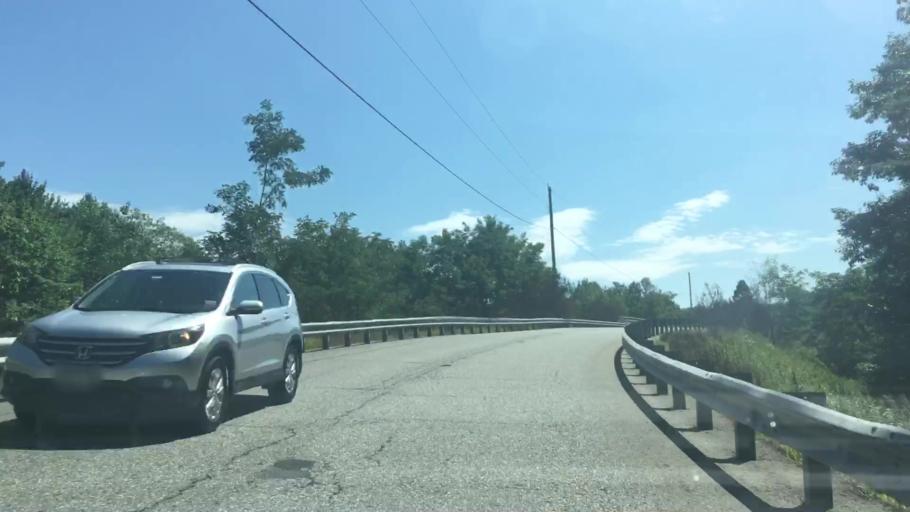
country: US
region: Maine
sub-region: Androscoggin County
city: Sabattus
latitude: 44.1250
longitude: -70.0362
